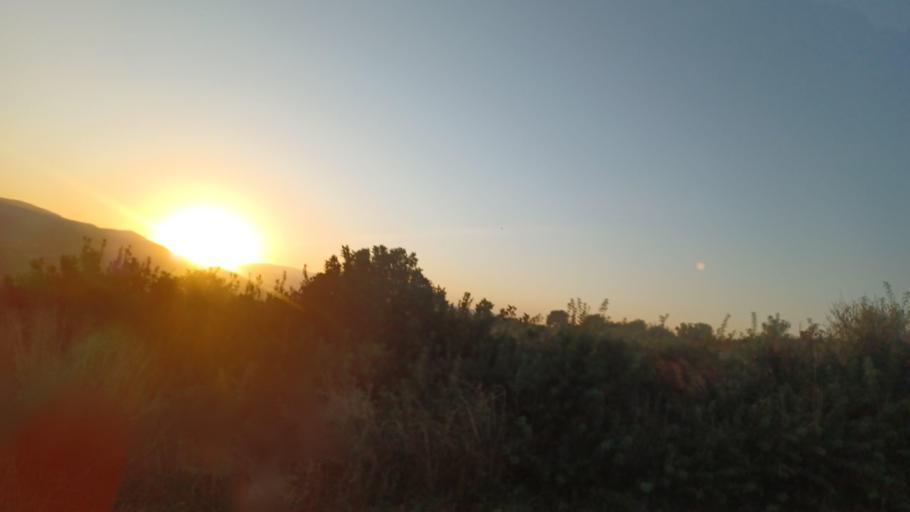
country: CY
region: Pafos
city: Polis
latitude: 34.9890
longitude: 32.4347
